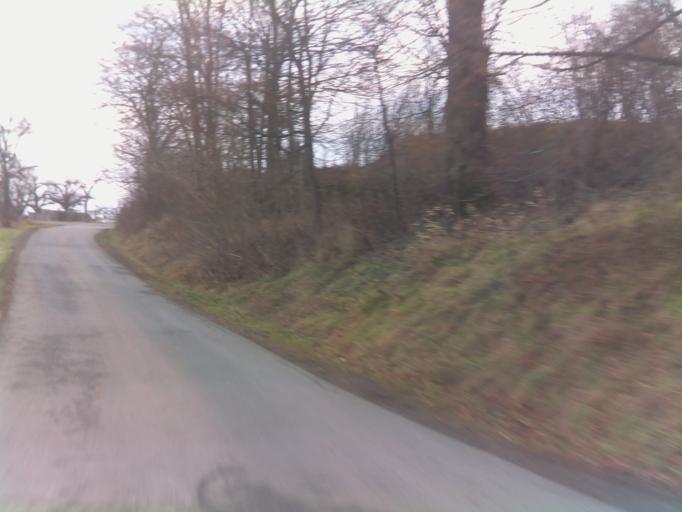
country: DE
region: Thuringia
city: Dreitzsch
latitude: 50.7277
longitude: 11.7877
